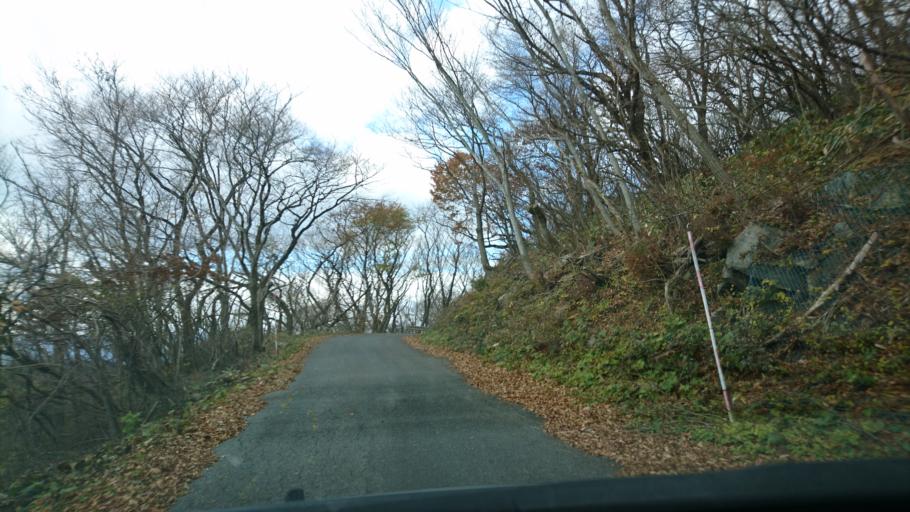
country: JP
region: Iwate
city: Ichinoseki
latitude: 39.0088
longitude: 141.1823
